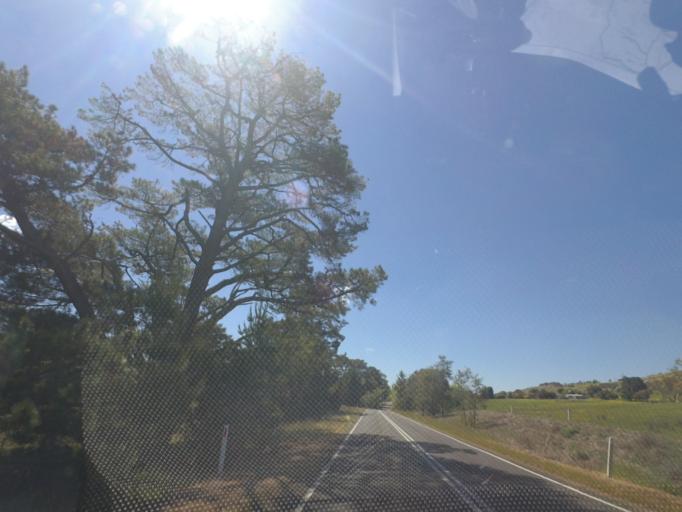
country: AU
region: Victoria
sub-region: Hume
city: Sunbury
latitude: -37.1021
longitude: 144.7591
